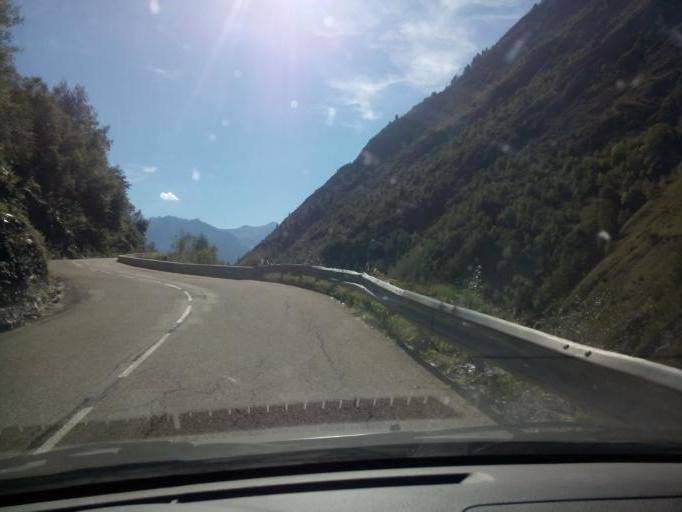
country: FR
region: Rhone-Alpes
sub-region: Departement de l'Isere
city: Mont-de-Lans
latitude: 45.0579
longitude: 6.1475
